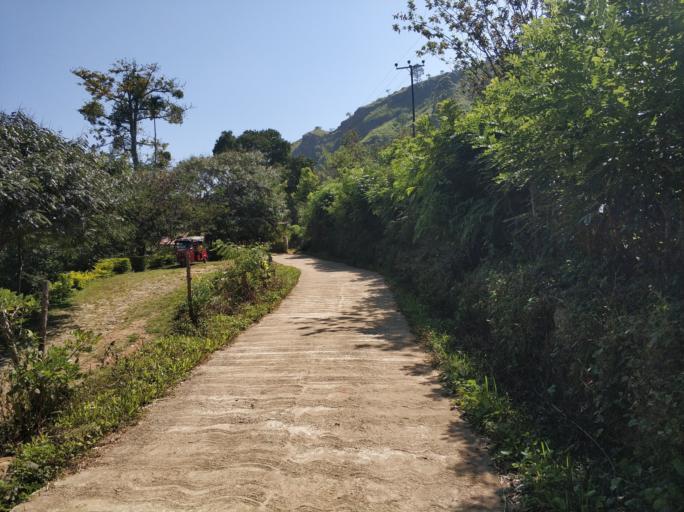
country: LK
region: Uva
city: Haputale
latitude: 6.8323
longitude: 81.0556
